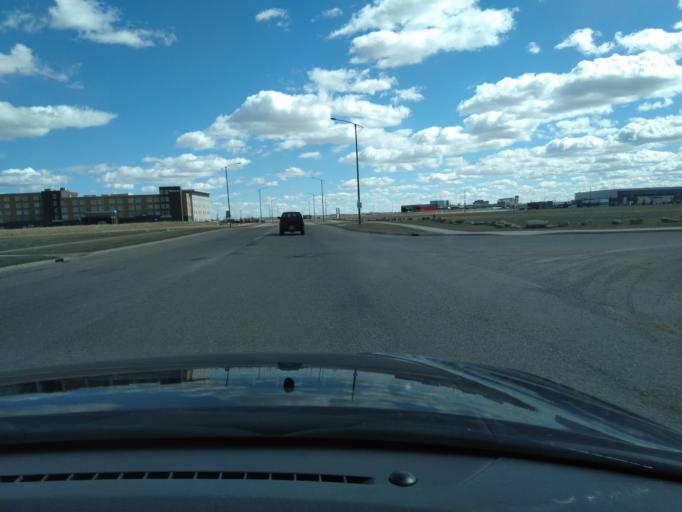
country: CA
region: Alberta
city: Calgary
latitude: 51.1365
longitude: -114.0326
